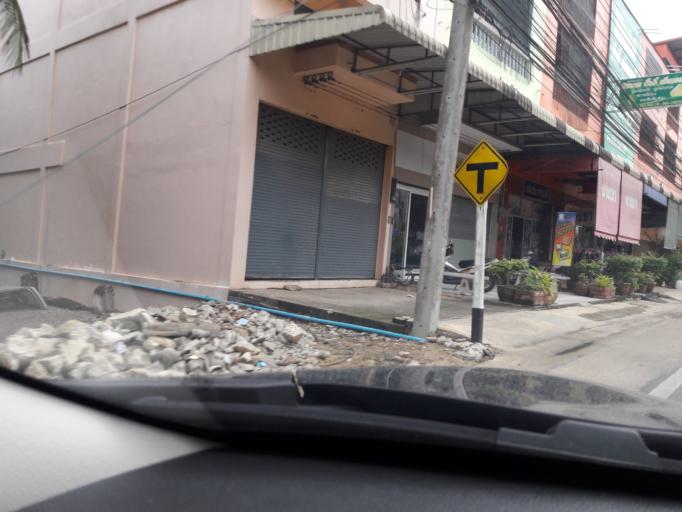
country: TH
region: Ratchaburi
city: Damnoen Saduak
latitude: 13.5298
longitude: 99.9660
